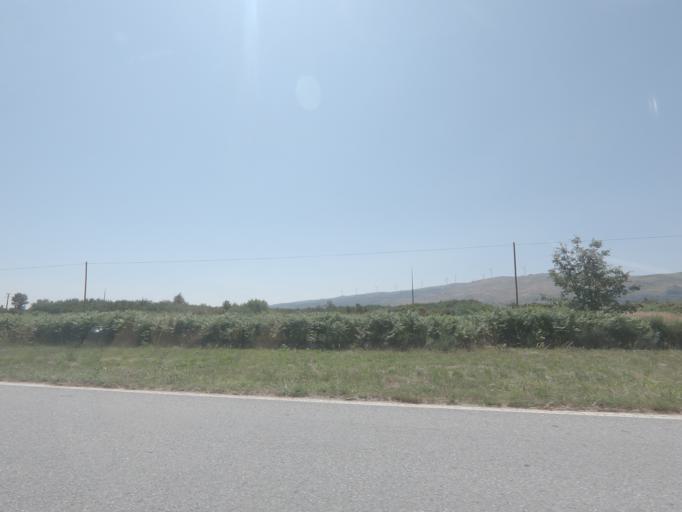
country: PT
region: Viseu
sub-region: Castro Daire
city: Castro Daire
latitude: 40.9680
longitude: -7.8840
